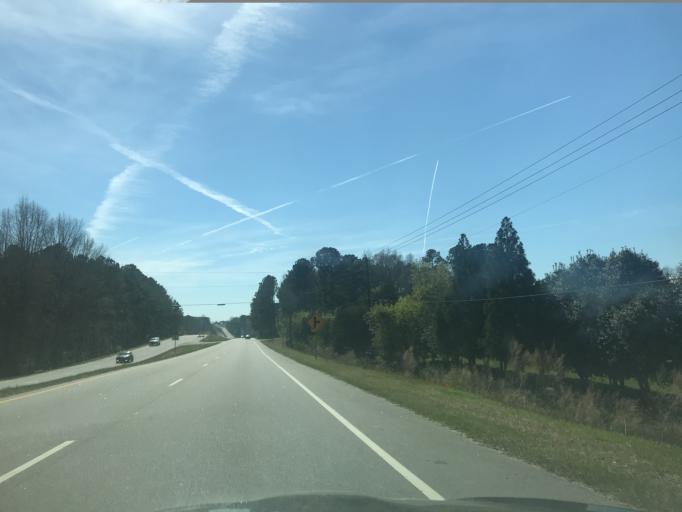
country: US
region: North Carolina
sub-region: Wake County
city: Fuquay-Varina
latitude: 35.6212
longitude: -78.7287
